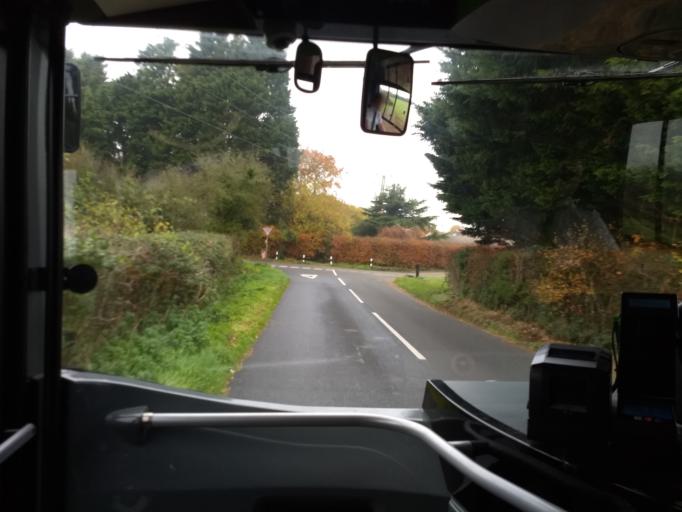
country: GB
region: England
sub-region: Isle of Wight
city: Newchurch
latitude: 50.6551
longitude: -1.2169
